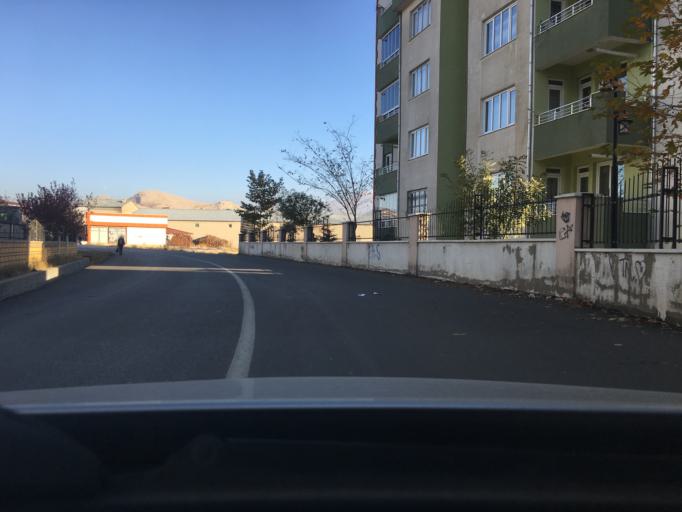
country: TR
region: Van
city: Van
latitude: 38.5220
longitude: 43.3561
